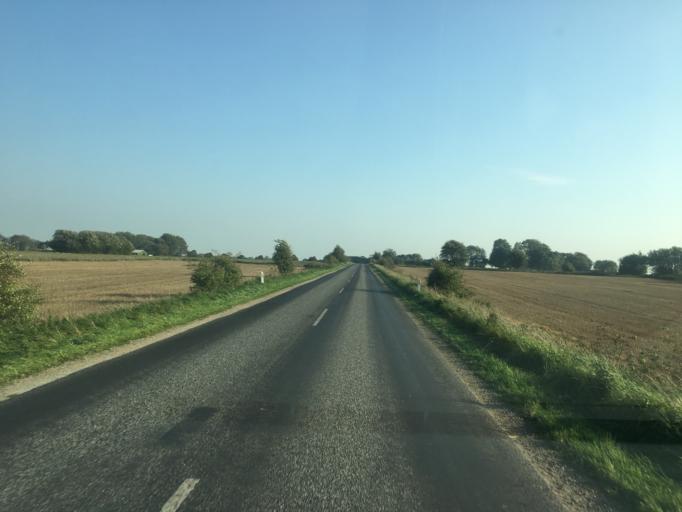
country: DE
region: Schleswig-Holstein
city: Bramstedtlund
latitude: 54.9531
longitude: 9.0558
